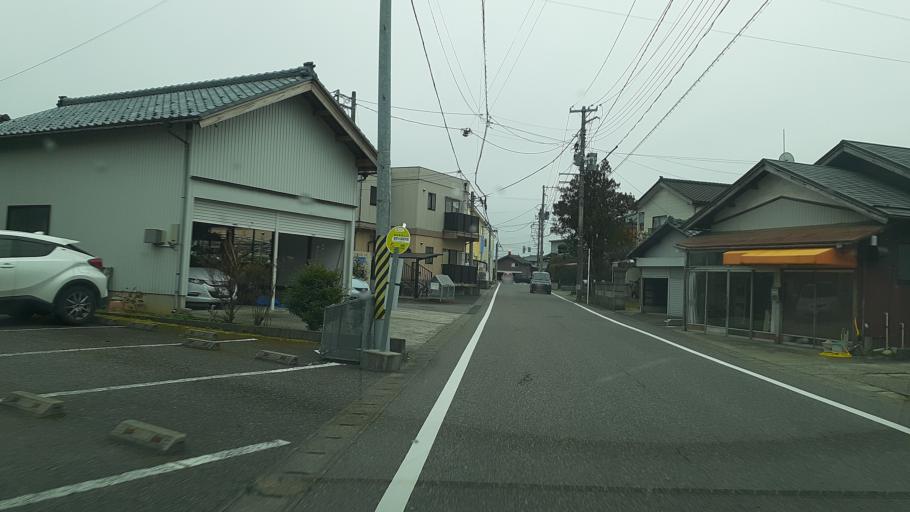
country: JP
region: Niigata
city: Niigata-shi
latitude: 37.8561
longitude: 139.0341
